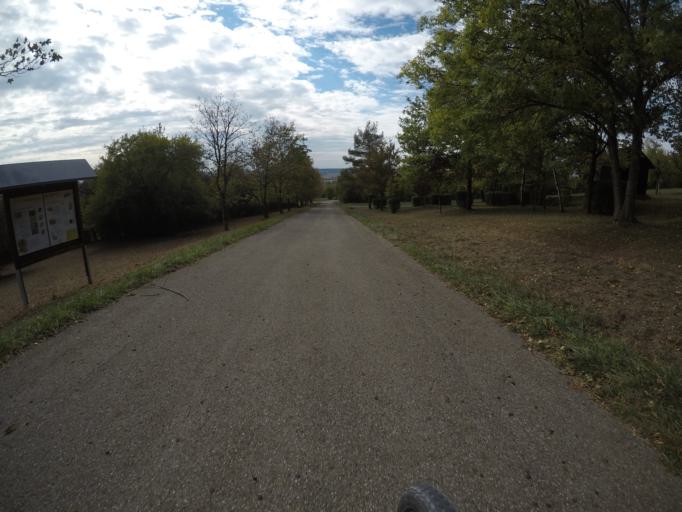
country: DE
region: Baden-Wuerttemberg
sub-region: Regierungsbezirk Stuttgart
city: Nufringen
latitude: 48.6017
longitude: 8.8939
